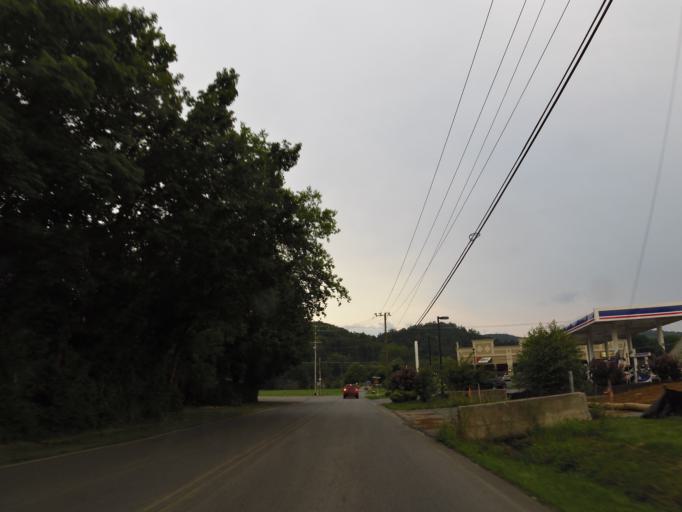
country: US
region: Tennessee
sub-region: Sevier County
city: Pigeon Forge
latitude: 35.7882
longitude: -83.6268
